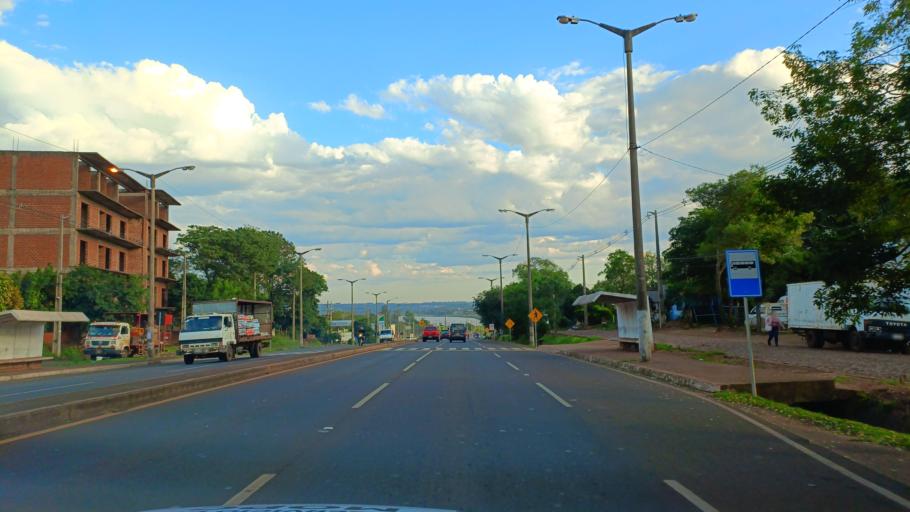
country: PY
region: Itapua
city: Encarnacion
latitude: -27.3068
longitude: -55.8908
